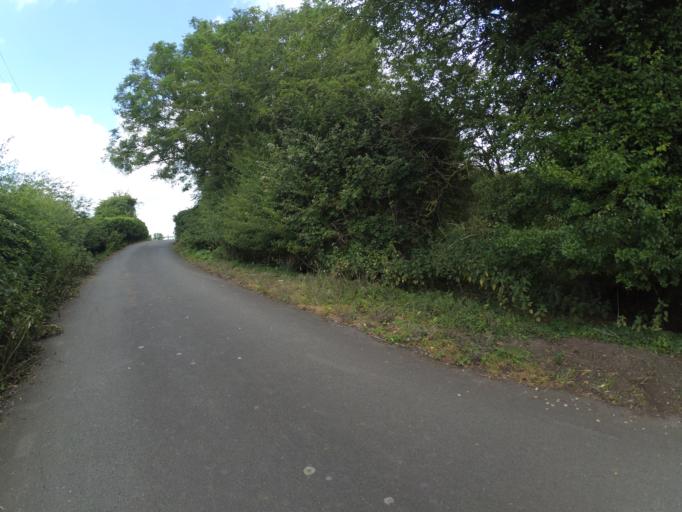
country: GB
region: England
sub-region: Warwickshire
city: Long Lawford
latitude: 52.3885
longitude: -1.2905
